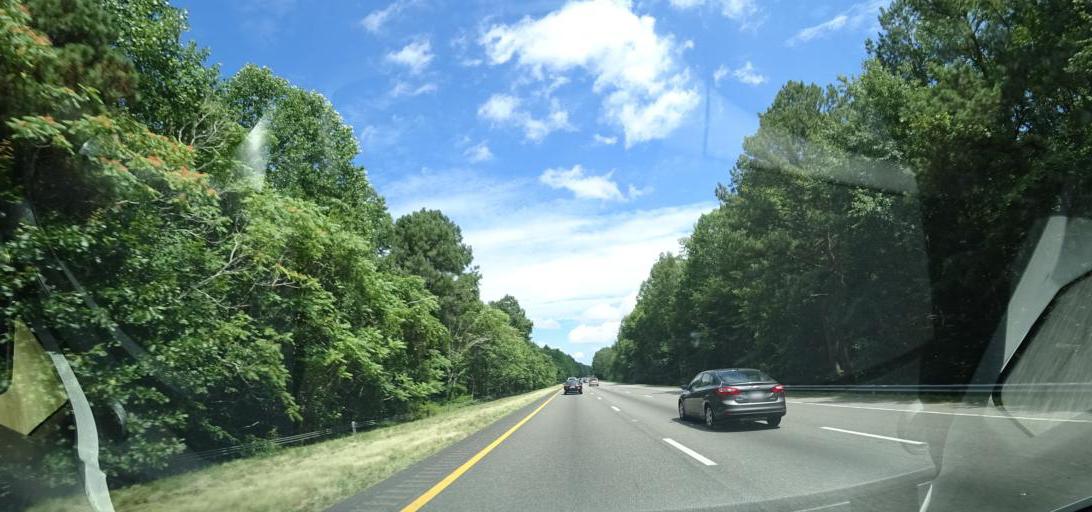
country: US
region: Virginia
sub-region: King William County
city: West Point
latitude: 37.4193
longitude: -76.8176
